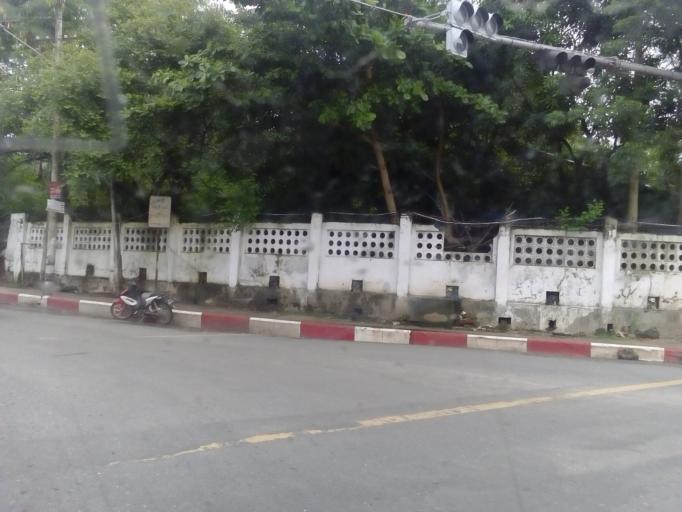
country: MM
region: Yangon
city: Yangon
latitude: 16.8501
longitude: 96.1576
